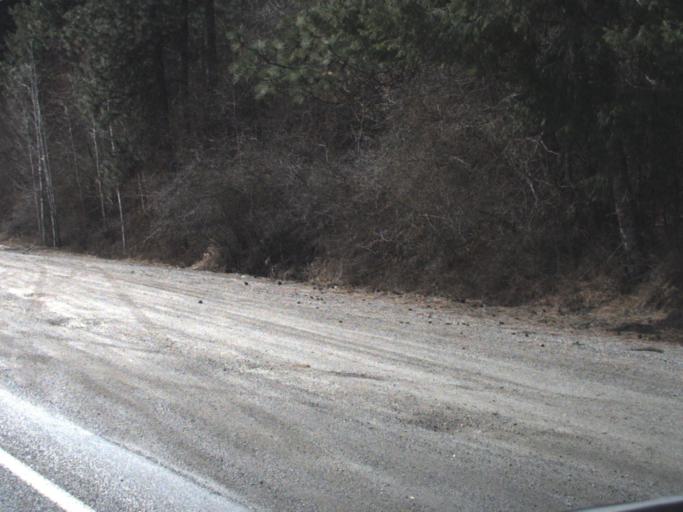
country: US
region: Washington
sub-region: Pend Oreille County
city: Newport
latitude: 48.4067
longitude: -117.3139
